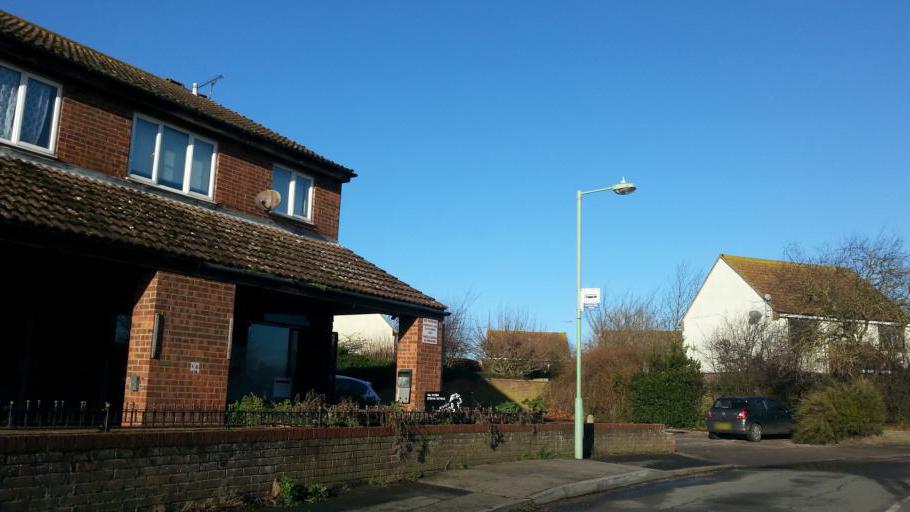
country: GB
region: England
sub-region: Suffolk
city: Felixstowe
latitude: 51.9806
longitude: 1.3226
